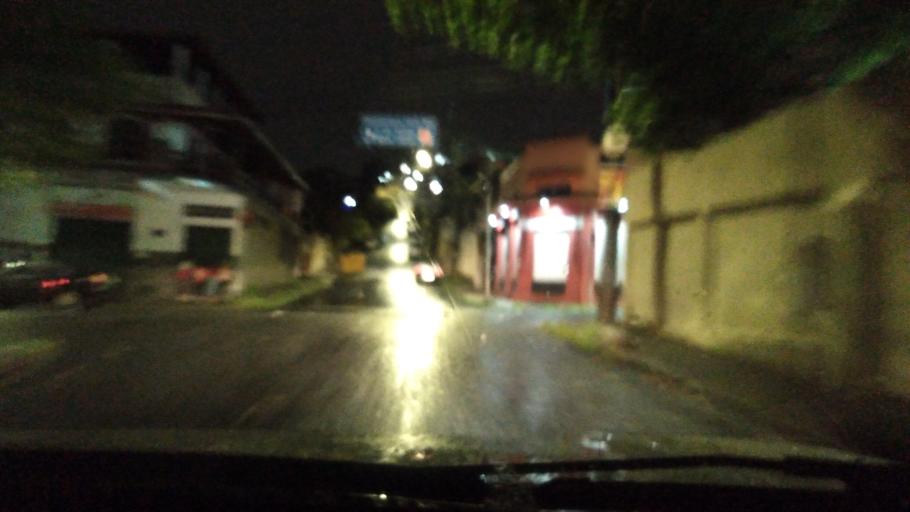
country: BR
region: Minas Gerais
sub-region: Belo Horizonte
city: Belo Horizonte
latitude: -19.8939
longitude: -43.9583
